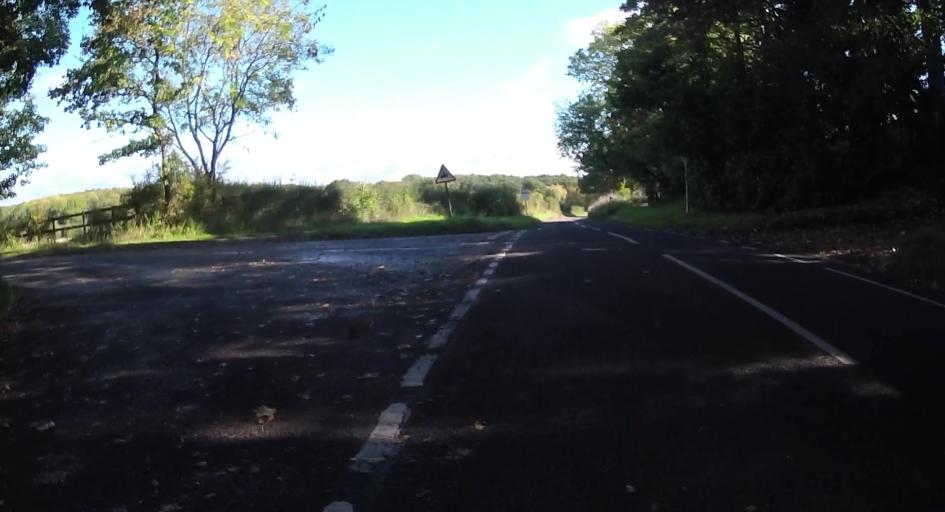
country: GB
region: England
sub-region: Hampshire
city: Old Basing
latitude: 51.2648
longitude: -1.0116
